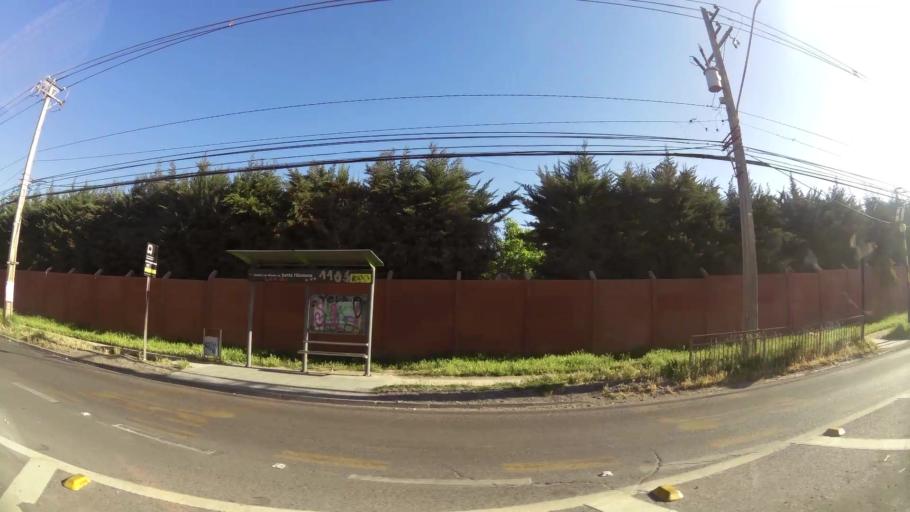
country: CL
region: Santiago Metropolitan
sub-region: Provincia de Maipo
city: San Bernardo
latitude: -33.6395
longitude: -70.7035
